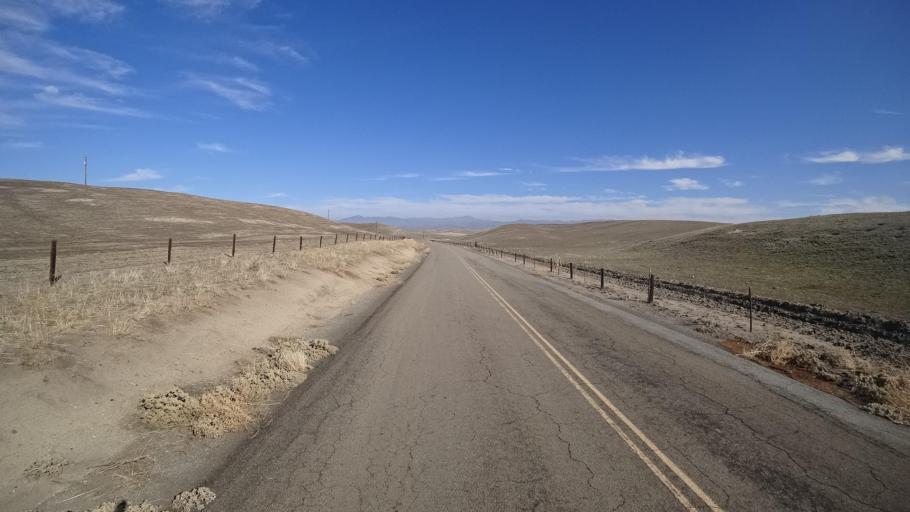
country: US
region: California
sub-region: Tulare County
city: Richgrove
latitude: 35.6346
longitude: -118.9523
